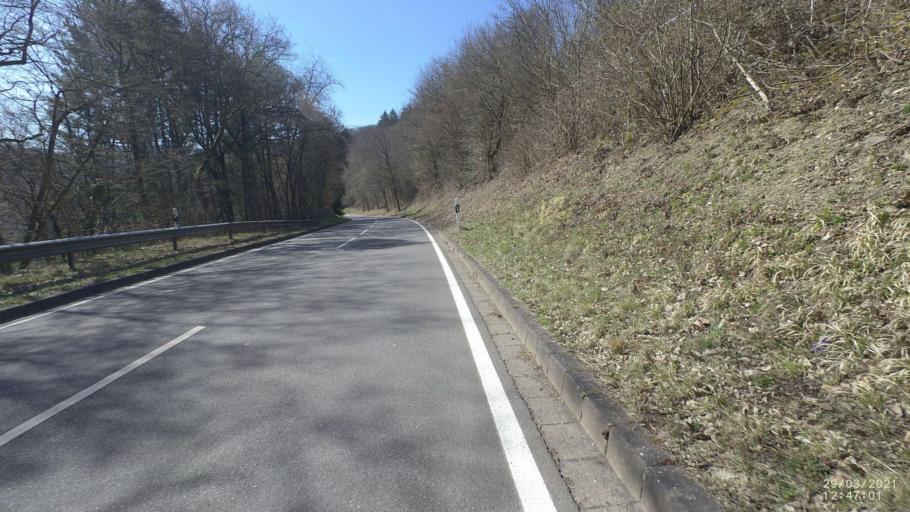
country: DE
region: Rheinland-Pfalz
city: Nickenich
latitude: 50.4459
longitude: 7.3190
